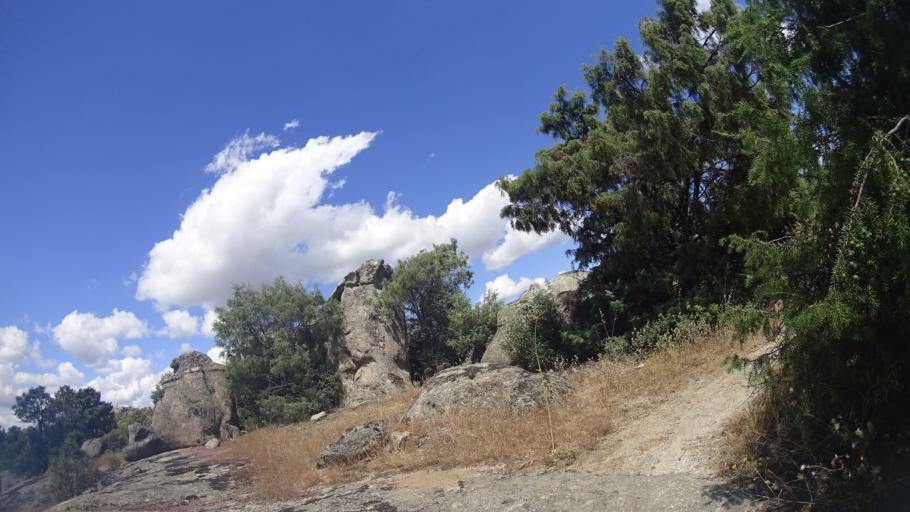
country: ES
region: Madrid
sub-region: Provincia de Madrid
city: Torrelodones
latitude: 40.6005
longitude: -3.9208
